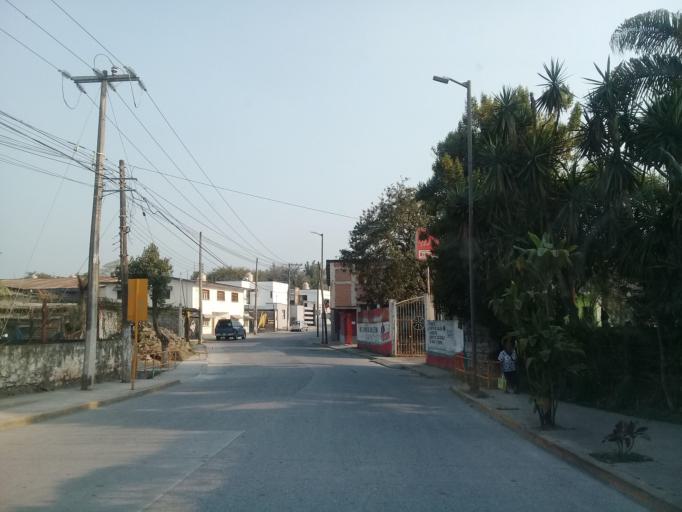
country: MX
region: Veracruz
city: Ixtac Zoquitlan
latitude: 18.8575
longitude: -97.0574
